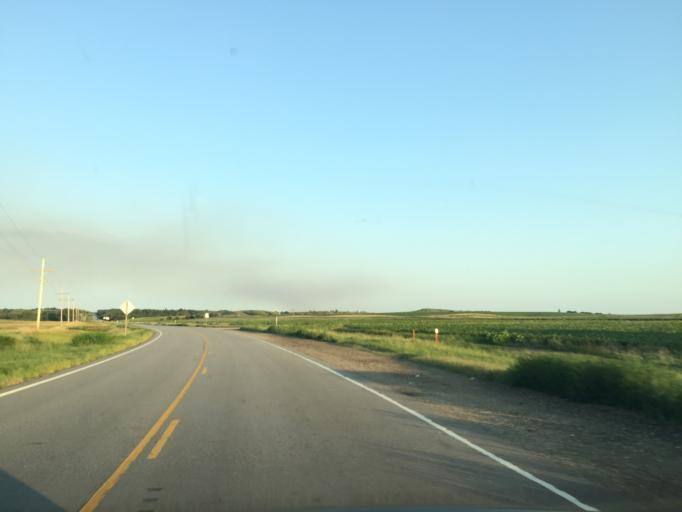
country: US
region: Kansas
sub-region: Ellsworth County
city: Ellsworth
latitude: 38.7107
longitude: -98.2333
